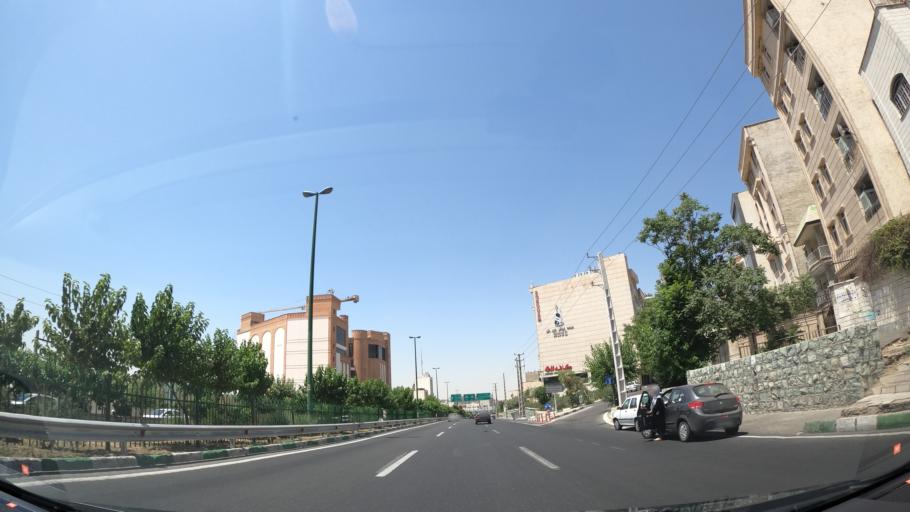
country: IR
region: Tehran
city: Tajrish
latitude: 35.7660
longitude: 51.3075
